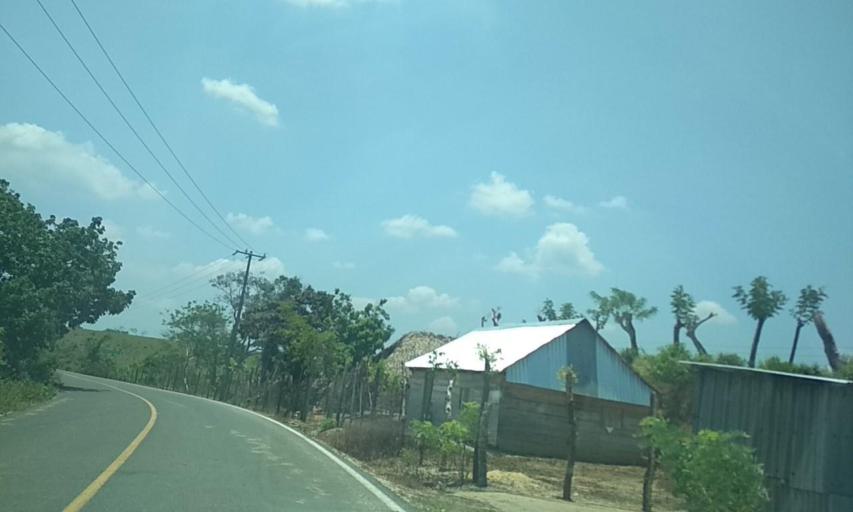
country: MX
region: Tabasco
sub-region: Huimanguillo
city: Francisco Rueda
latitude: 17.7635
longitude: -94.0591
